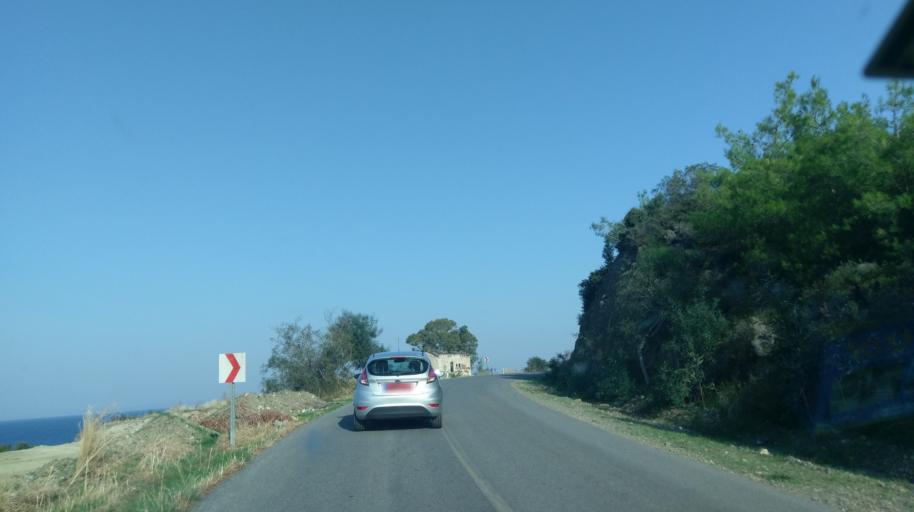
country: CY
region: Lefkosia
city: Lefka
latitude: 35.1541
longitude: 32.7886
